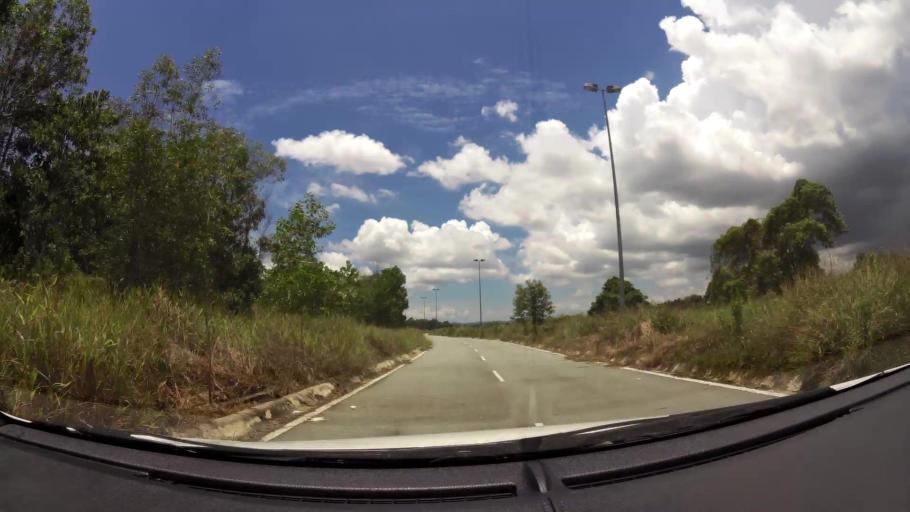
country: BN
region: Brunei and Muara
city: Bandar Seri Begawan
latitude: 4.9413
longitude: 114.8837
